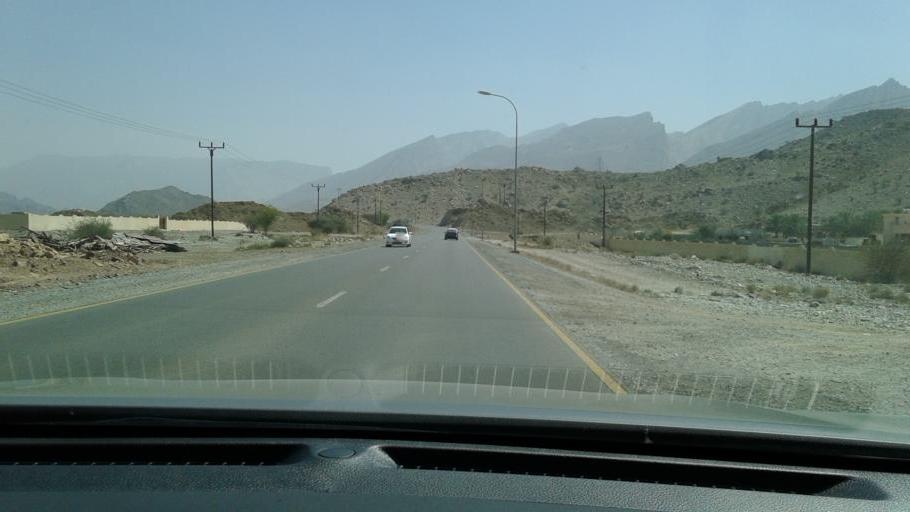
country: OM
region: Al Batinah
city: Rustaq
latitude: 23.3735
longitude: 57.4541
